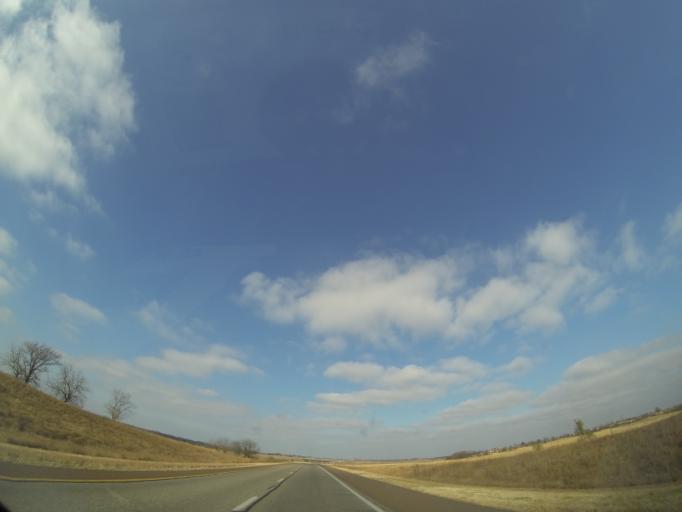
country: US
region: Kansas
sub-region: McPherson County
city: Lindsborg
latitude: 38.5168
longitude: -97.6199
